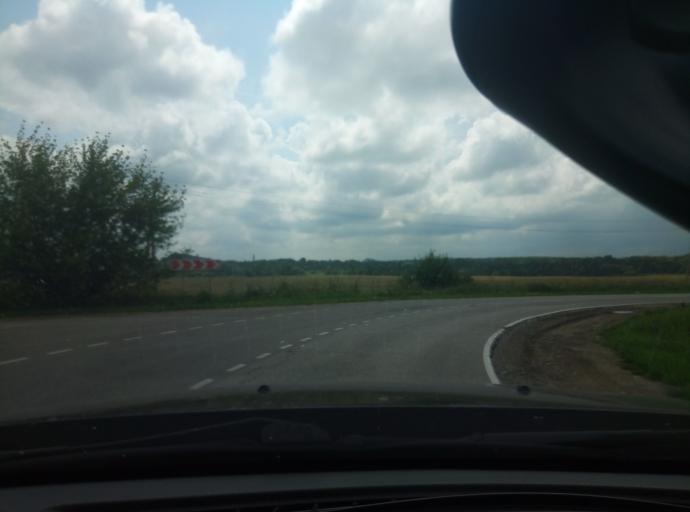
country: RU
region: Tula
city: Borodinskiy
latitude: 53.9861
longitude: 37.7880
